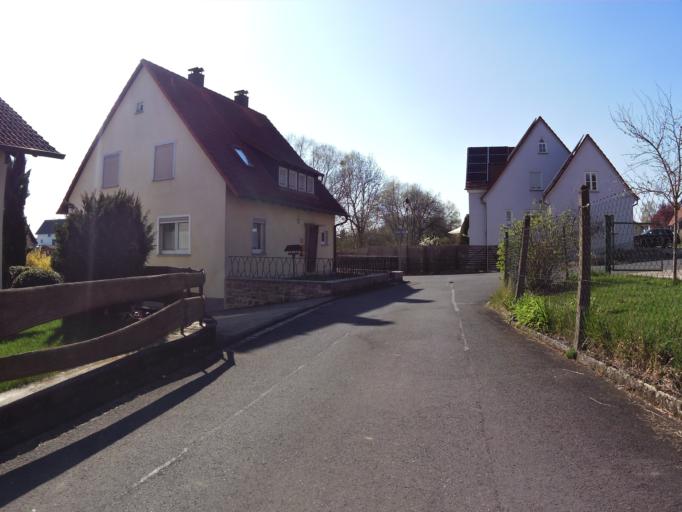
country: DE
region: Bavaria
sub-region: Regierungsbezirk Unterfranken
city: Prosselsheim
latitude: 49.8225
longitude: 10.1037
